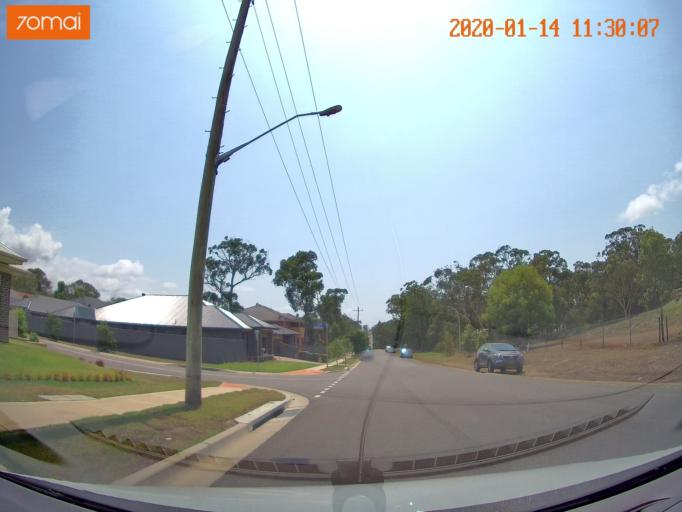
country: AU
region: New South Wales
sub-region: Lake Macquarie Shire
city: Dora Creek
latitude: -33.1057
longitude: 151.4778
